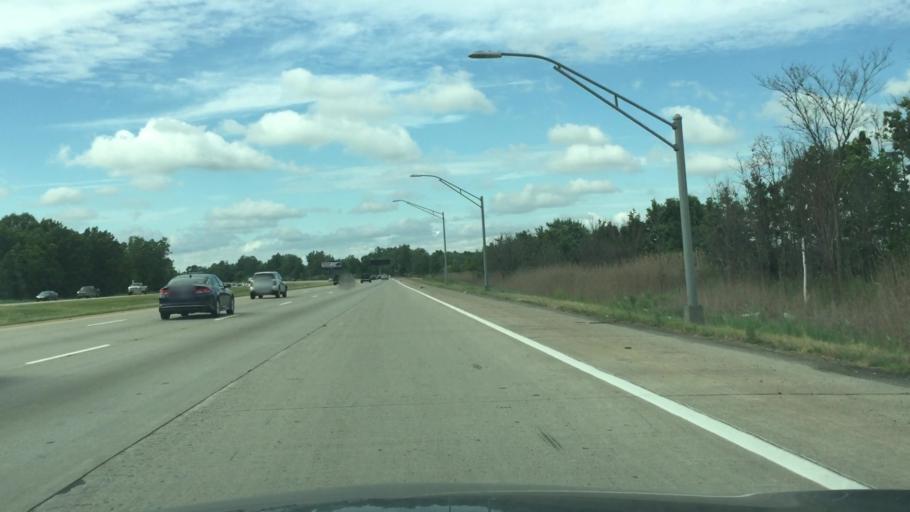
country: US
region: Michigan
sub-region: Wayne County
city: Romulus
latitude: 42.2002
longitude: -83.3886
